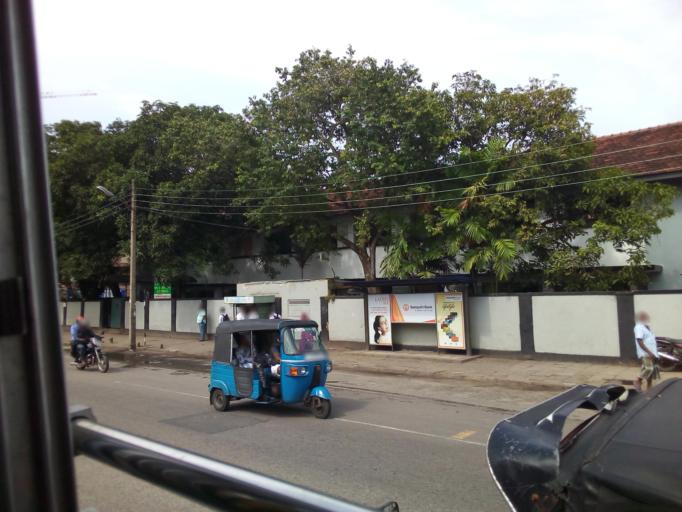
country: LK
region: Western
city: Colombo
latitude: 6.9215
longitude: 79.8529
